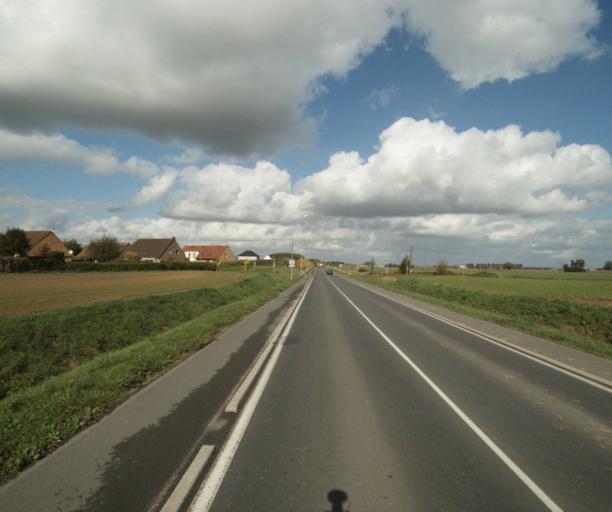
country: FR
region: Nord-Pas-de-Calais
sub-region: Departement du Nord
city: Houplines
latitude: 50.6911
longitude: 2.9217
